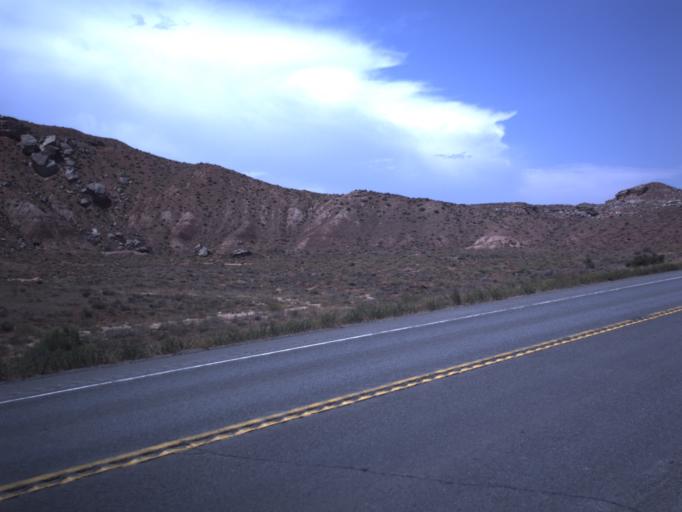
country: US
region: Utah
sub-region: Uintah County
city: Maeser
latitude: 40.3133
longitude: -109.7092
